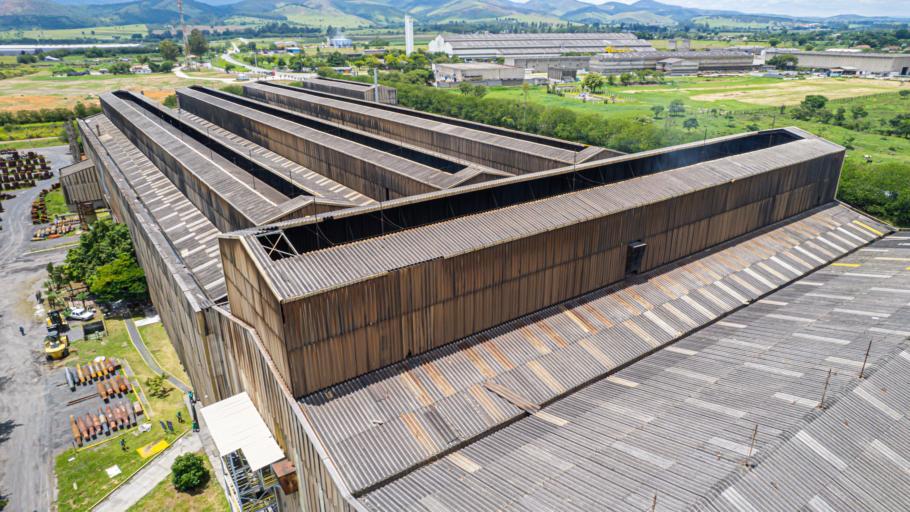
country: BR
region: Sao Paulo
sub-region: Pindamonhangaba
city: Pindamonhangaba
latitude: -22.9067
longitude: -45.3517
